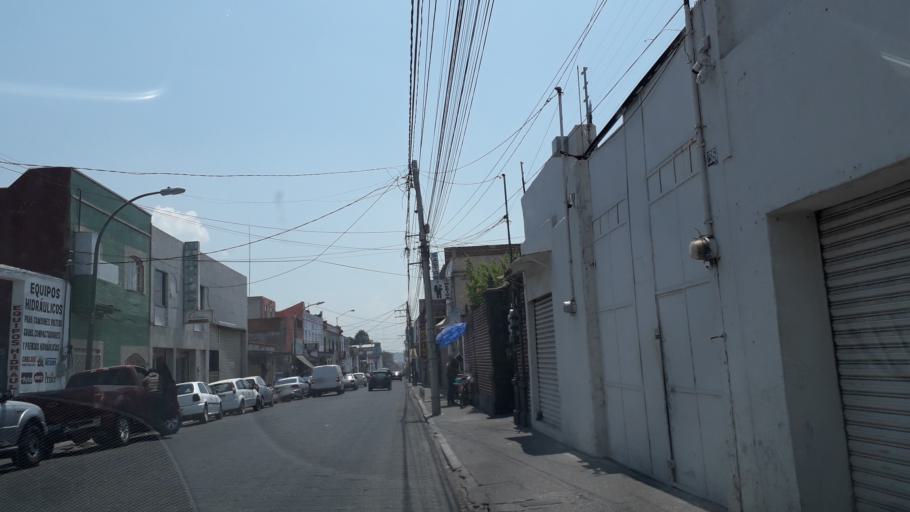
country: MX
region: Puebla
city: Puebla
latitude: 19.0535
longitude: -98.2165
